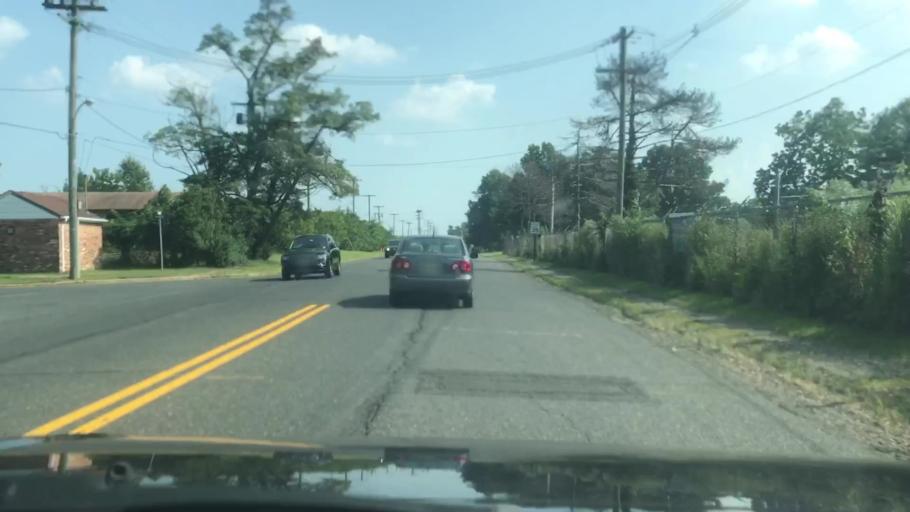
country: US
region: New Jersey
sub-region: Monmouth County
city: Little Silver
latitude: 40.3208
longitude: -74.0359
